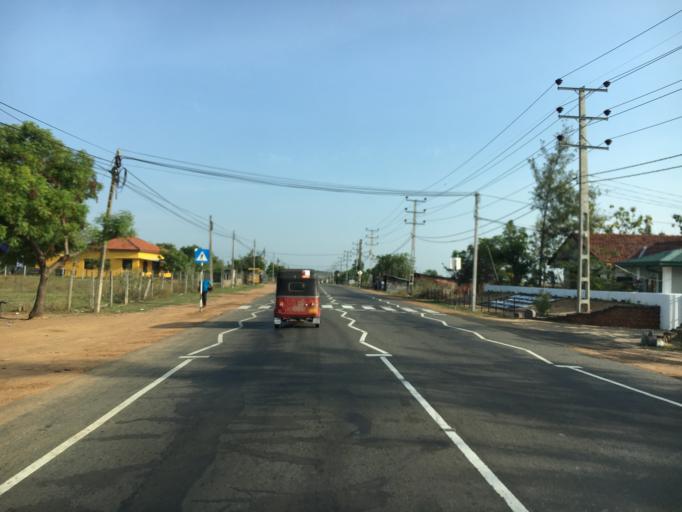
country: LK
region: Eastern Province
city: Eravur Town
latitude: 7.9315
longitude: 81.5118
